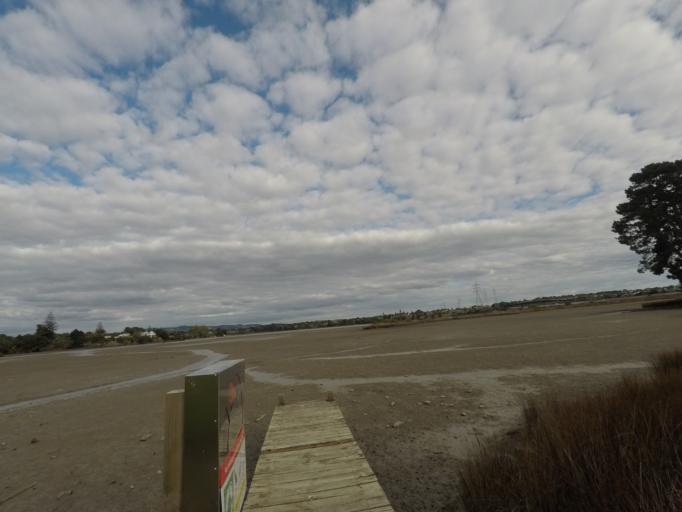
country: NZ
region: Auckland
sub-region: Auckland
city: Papakura
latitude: -37.0549
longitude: 174.9243
